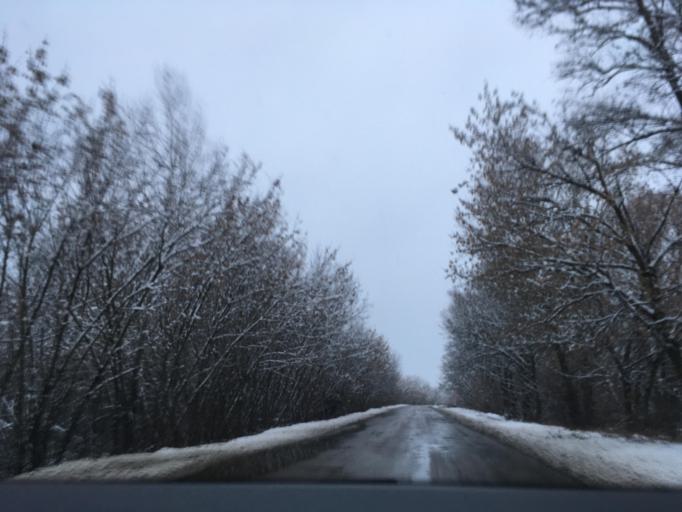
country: RU
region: Voronezj
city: Mitrofanovka
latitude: 50.1335
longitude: 39.9932
